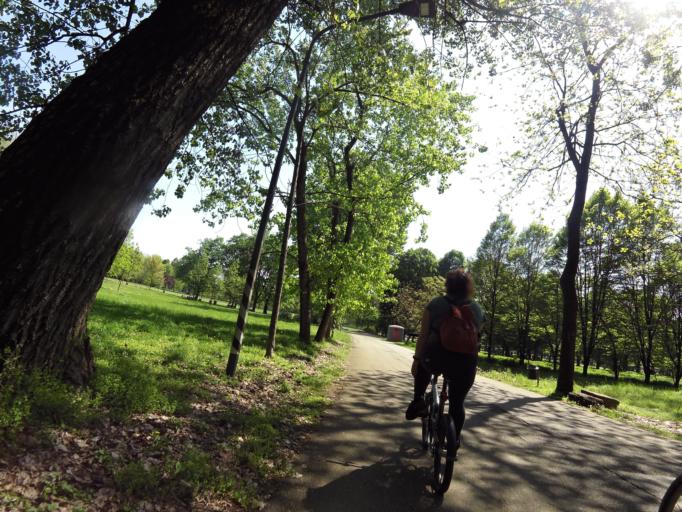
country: IT
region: Lombardy
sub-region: Citta metropolitana di Milano
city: Sesto San Giovanni
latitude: 45.4971
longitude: 9.2491
